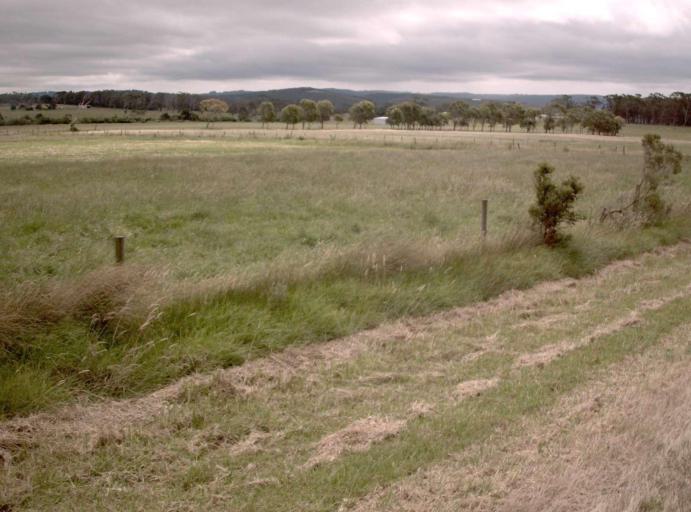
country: AU
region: Victoria
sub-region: Latrobe
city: Traralgon
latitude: -38.5483
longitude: 146.6550
